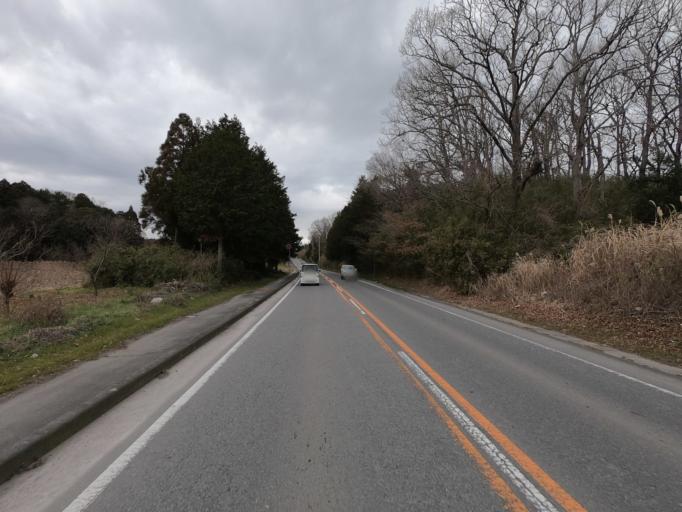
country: JP
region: Ibaraki
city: Ishioka
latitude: 36.0949
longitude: 140.3673
